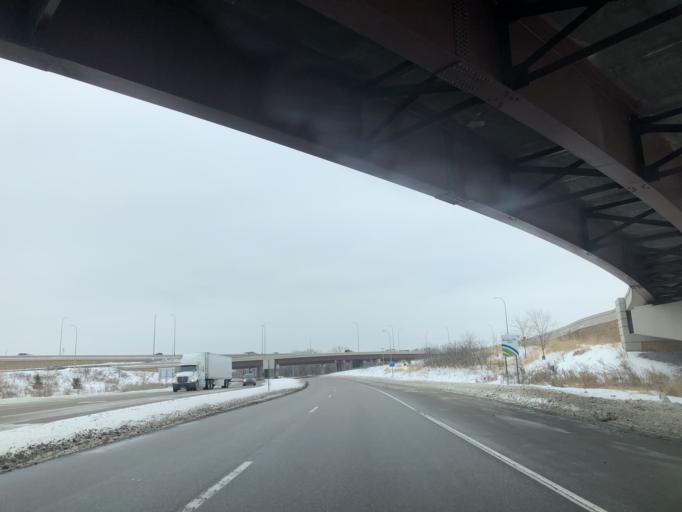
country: US
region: Minnesota
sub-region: Hennepin County
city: Osseo
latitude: 45.1082
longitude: -93.3945
